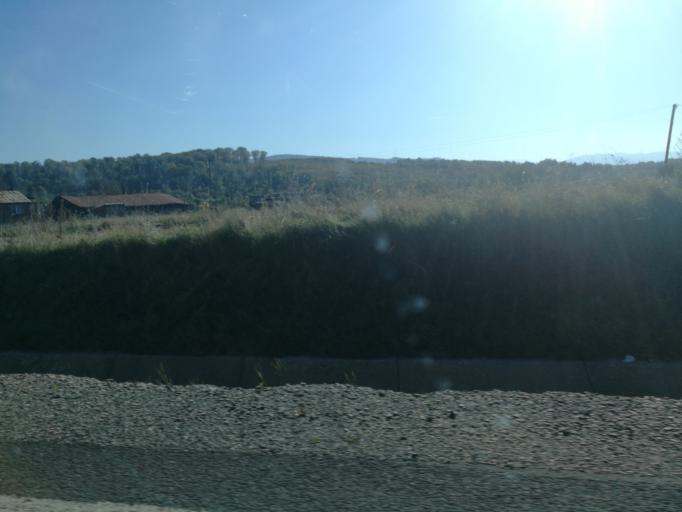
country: RO
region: Brasov
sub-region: Comuna Dumbravita
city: Dumbravita
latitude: 45.7696
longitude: 25.3611
